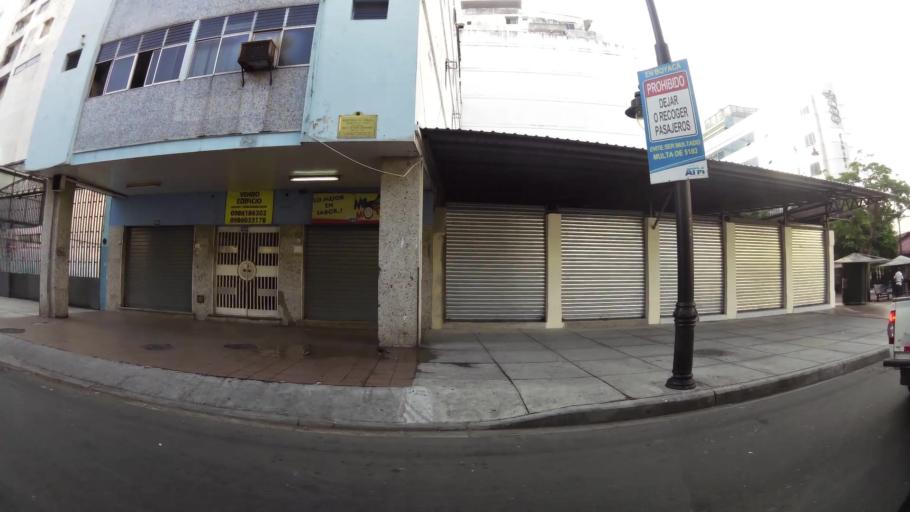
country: EC
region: Guayas
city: Guayaquil
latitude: -2.1969
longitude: -79.8852
